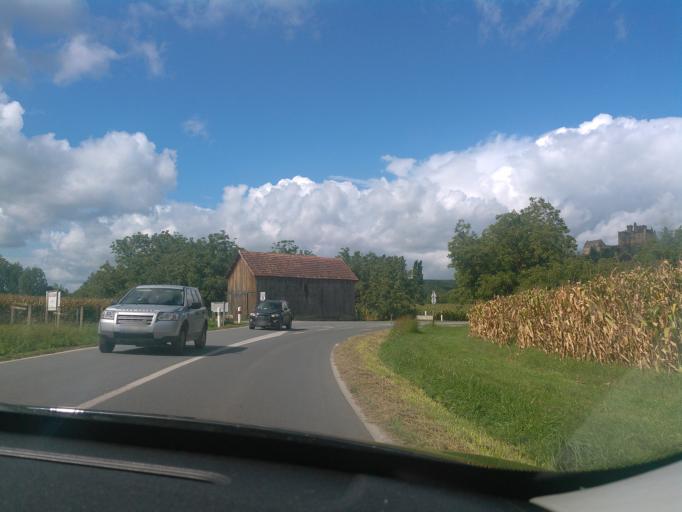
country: FR
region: Aquitaine
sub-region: Departement de la Dordogne
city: Cenac-et-Saint-Julien
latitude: 44.8339
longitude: 1.1533
